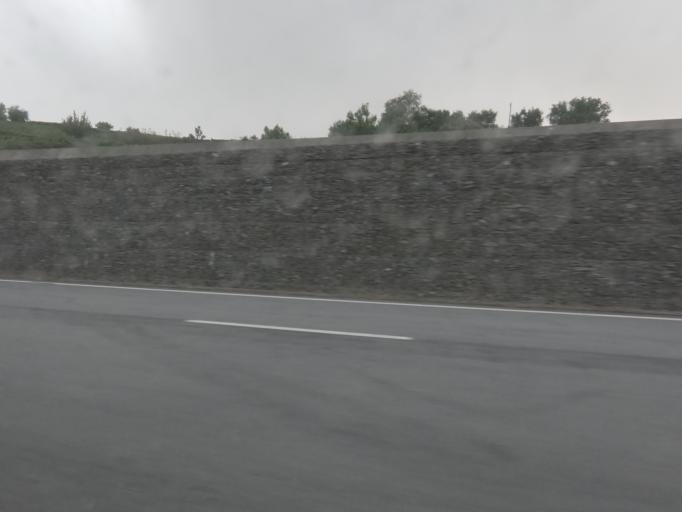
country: PT
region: Vila Real
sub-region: Peso da Regua
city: Peso da Regua
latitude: 41.1826
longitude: -7.7505
